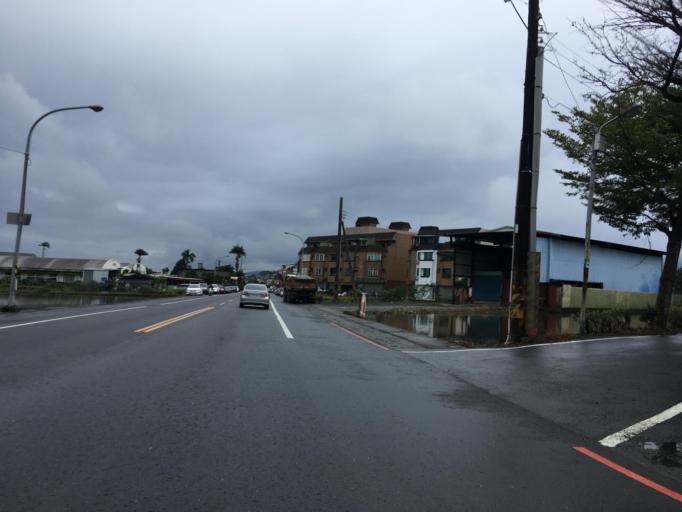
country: TW
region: Taiwan
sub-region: Yilan
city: Yilan
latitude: 24.6581
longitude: 121.7578
